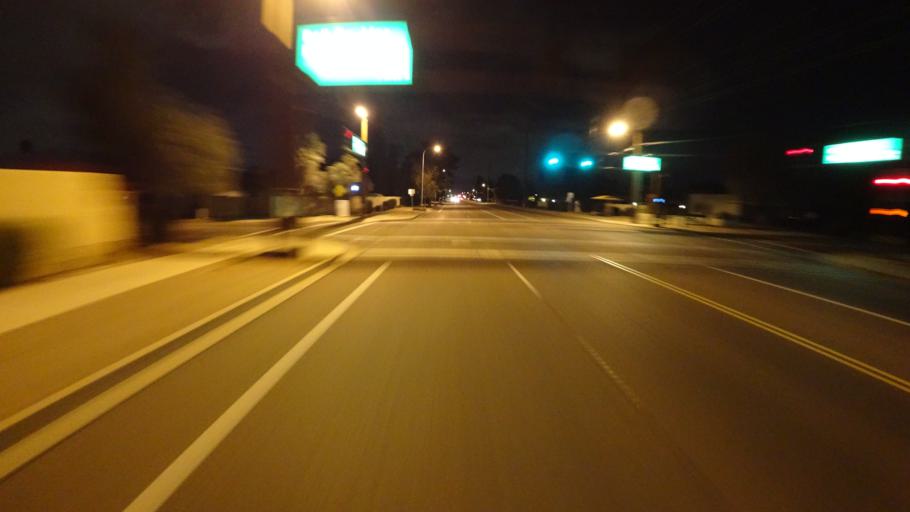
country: US
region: Arizona
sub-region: Maricopa County
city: Guadalupe
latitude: 33.3578
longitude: -111.9287
